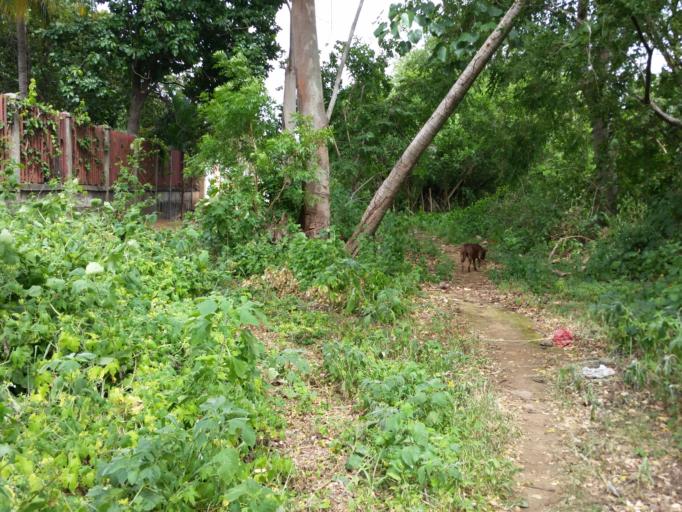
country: NI
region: Managua
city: Managua
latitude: 12.0764
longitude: -86.2503
